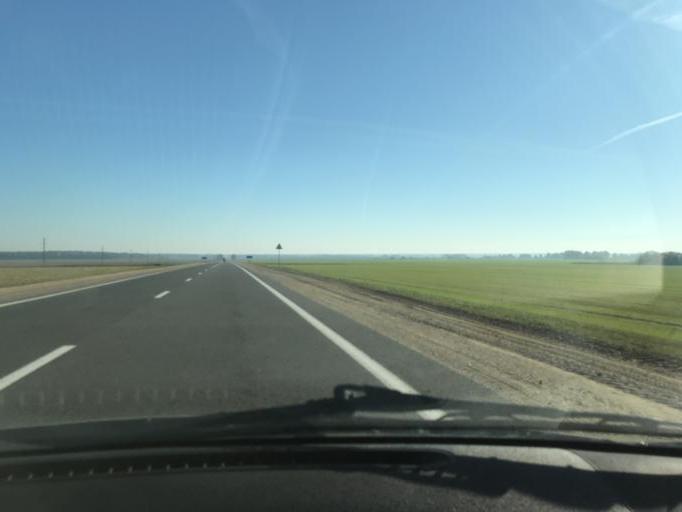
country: BY
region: Brest
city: Ivanava
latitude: 52.1562
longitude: 25.6453
